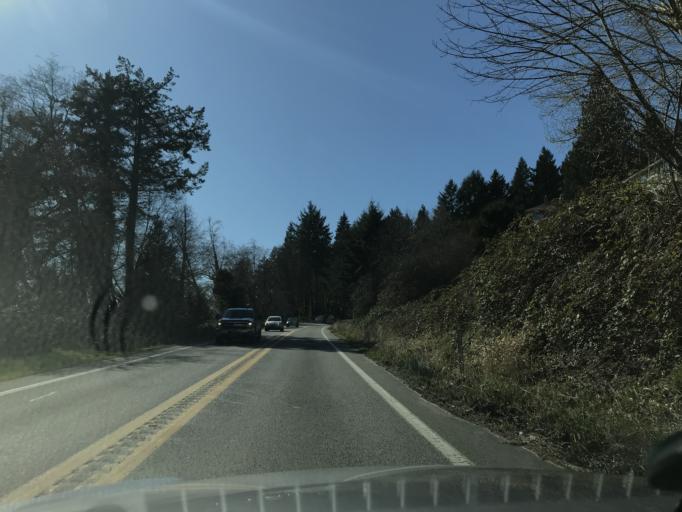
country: US
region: Washington
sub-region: Pierce County
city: Wauna
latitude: 47.3778
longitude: -122.6504
